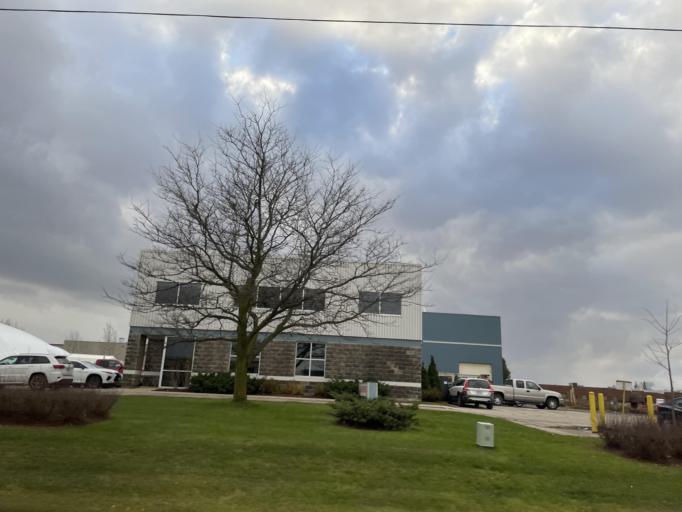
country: CA
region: Ontario
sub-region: Wellington County
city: Guelph
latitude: 43.5420
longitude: -80.3038
